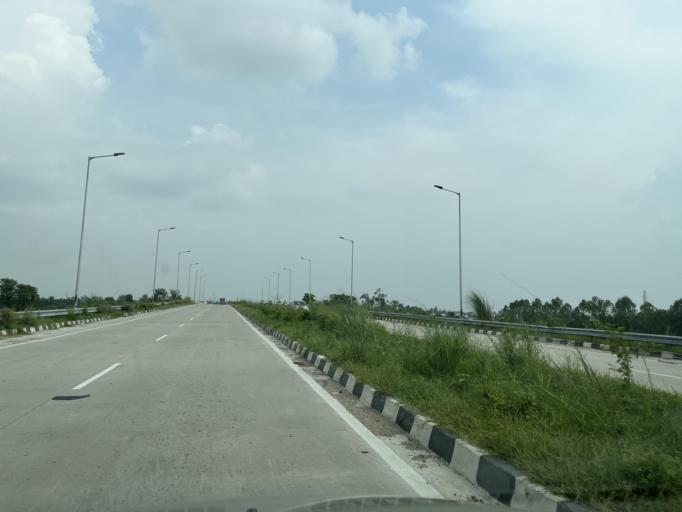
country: IN
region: Uttarakhand
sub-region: Udham Singh Nagar
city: Kashipur
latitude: 29.1749
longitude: 78.9439
